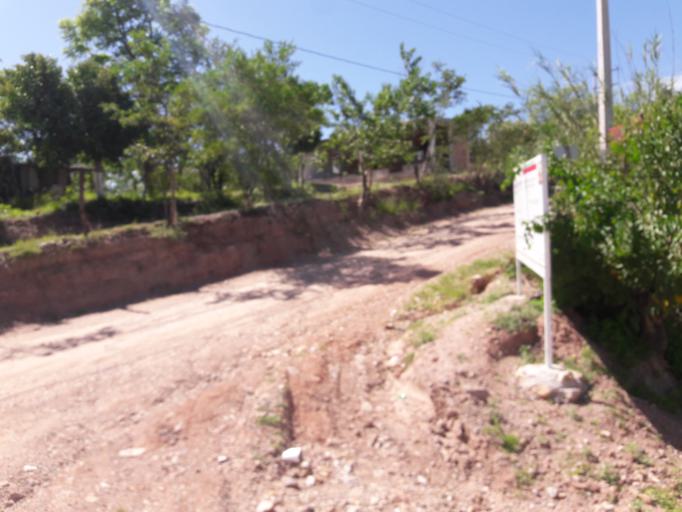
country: MX
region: Oaxaca
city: Ciudad de Huajuapam de Leon
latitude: 17.7996
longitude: -97.8006
